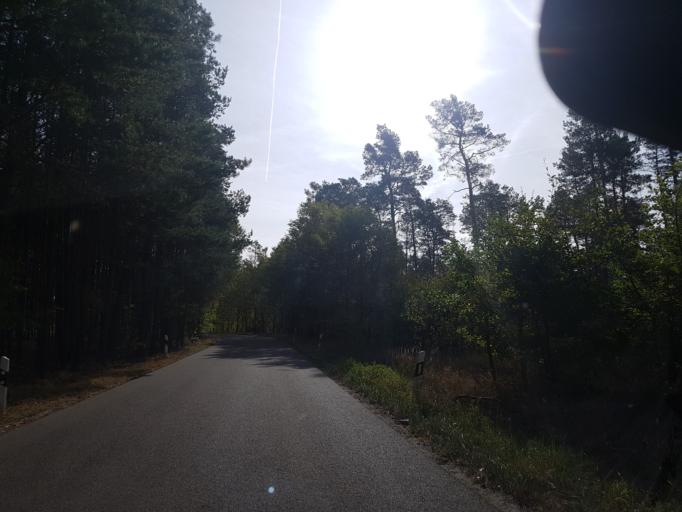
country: DE
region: Brandenburg
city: Schlieben
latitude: 51.7642
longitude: 13.3404
